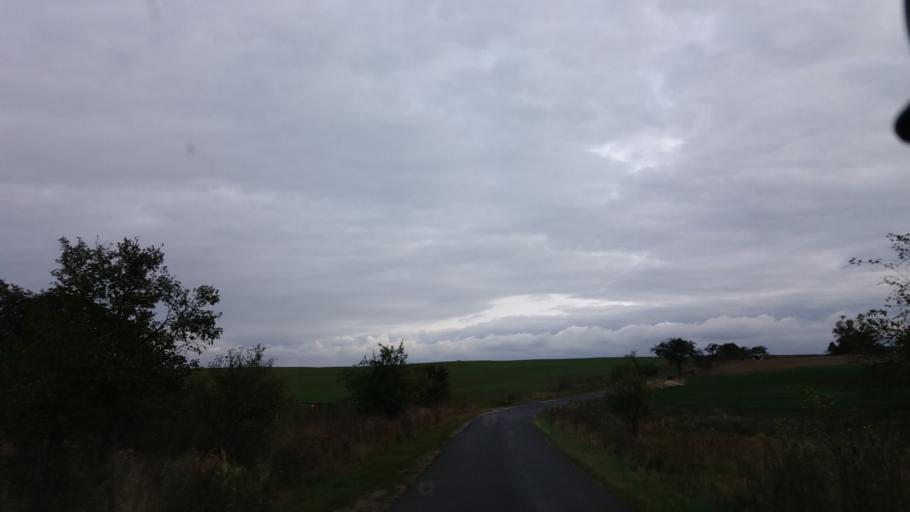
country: PL
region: West Pomeranian Voivodeship
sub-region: Powiat choszczenski
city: Pelczyce
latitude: 53.0326
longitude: 15.3199
